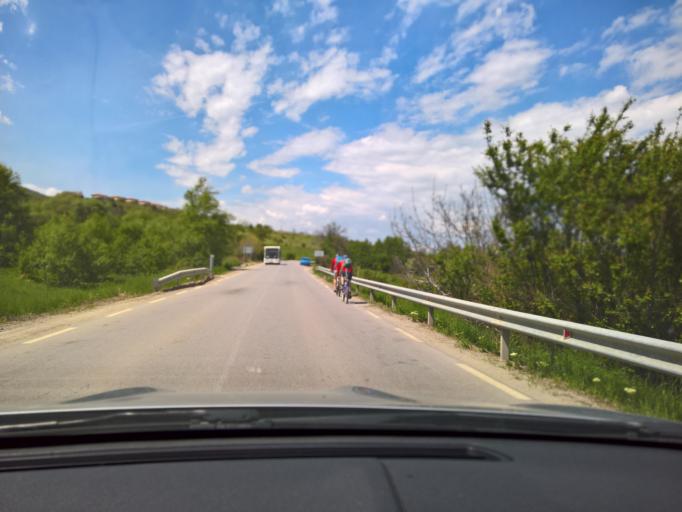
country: BG
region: Sofia-Capital
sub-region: Stolichna Obshtina
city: Sofia
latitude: 42.5734
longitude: 23.3586
